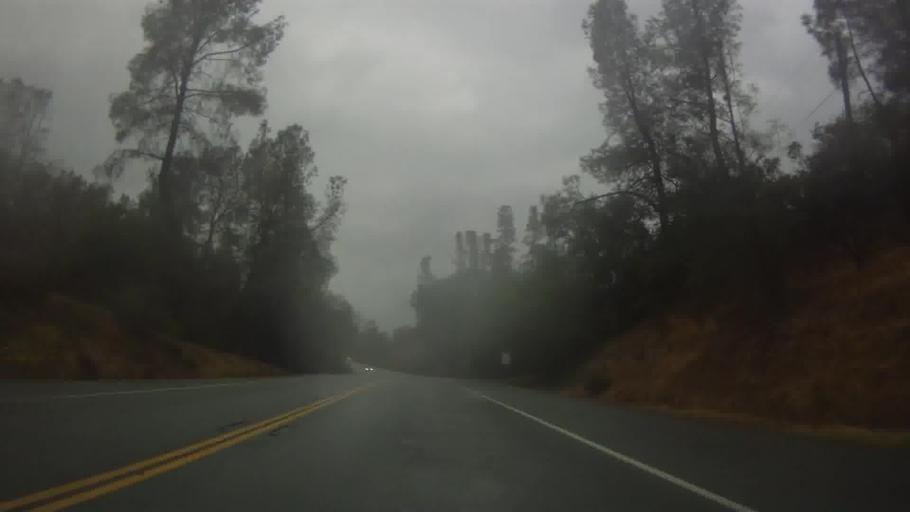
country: US
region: California
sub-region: Shasta County
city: Shasta
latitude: 40.5939
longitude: -122.4856
